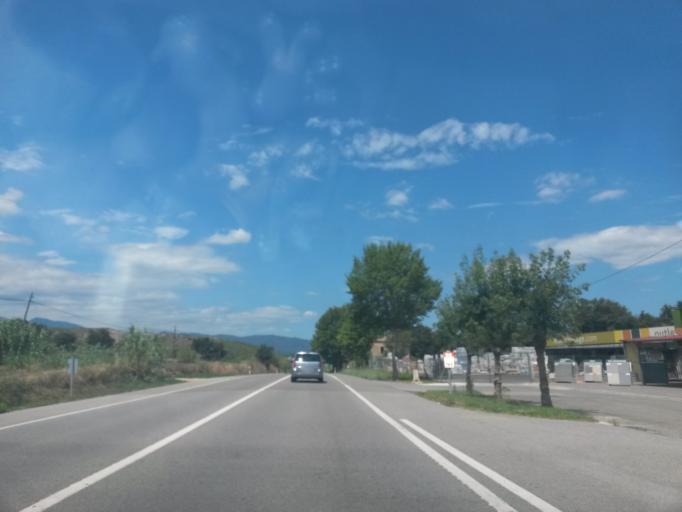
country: ES
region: Catalonia
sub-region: Provincia de Girona
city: Biure
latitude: 42.3385
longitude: 2.9191
